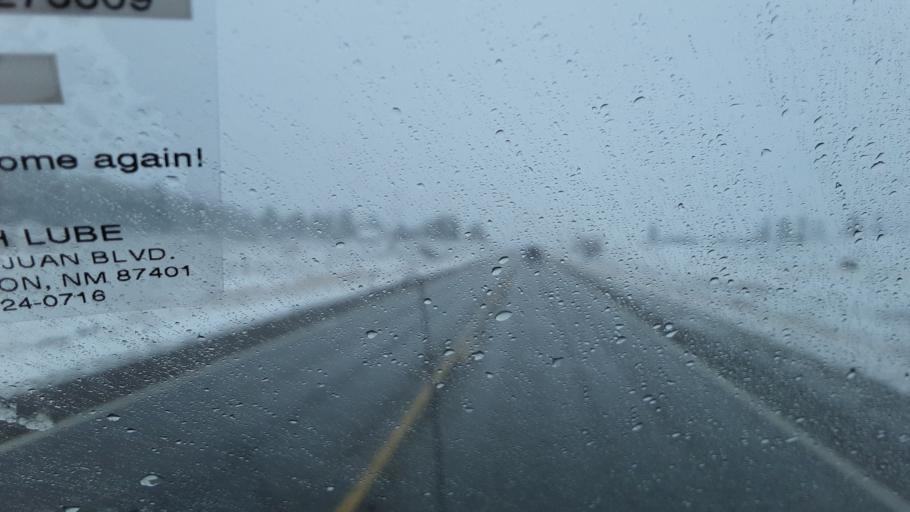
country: US
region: Colorado
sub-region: Archuleta County
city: Pagosa Springs
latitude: 37.2579
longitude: -106.9941
